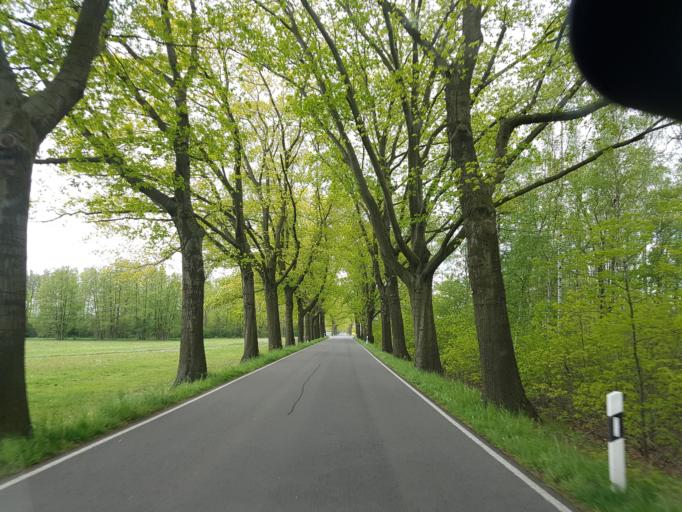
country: DE
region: Brandenburg
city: Bronkow
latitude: 51.6205
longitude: 13.9217
